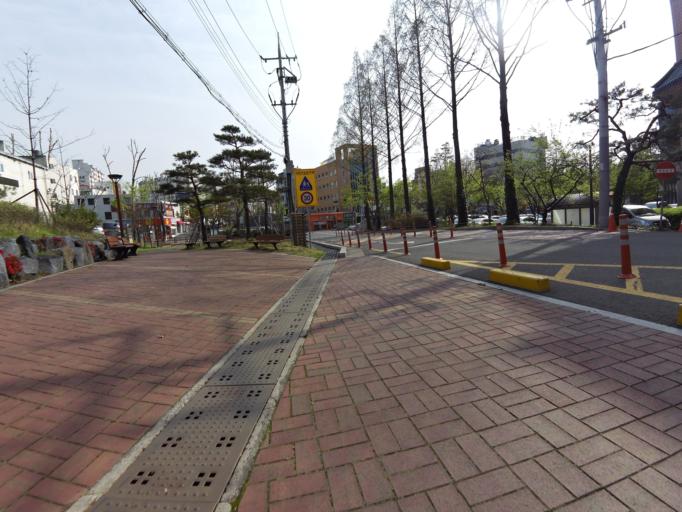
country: KR
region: Daegu
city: Daegu
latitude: 35.8867
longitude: 128.6363
